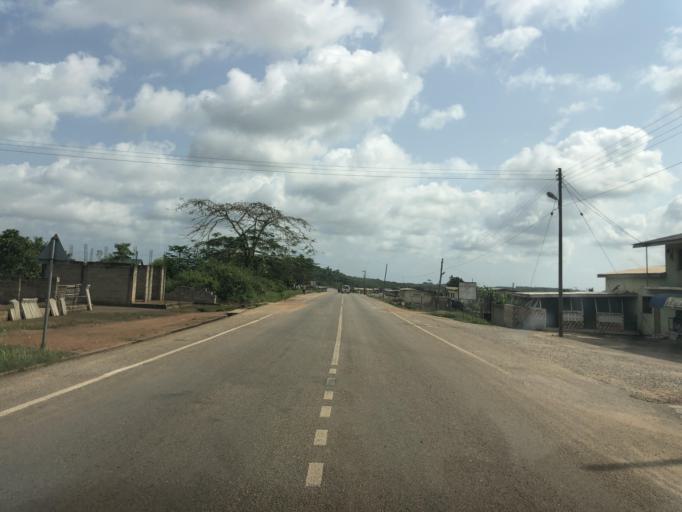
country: GH
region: Central
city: Elmina
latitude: 5.1972
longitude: -1.3201
